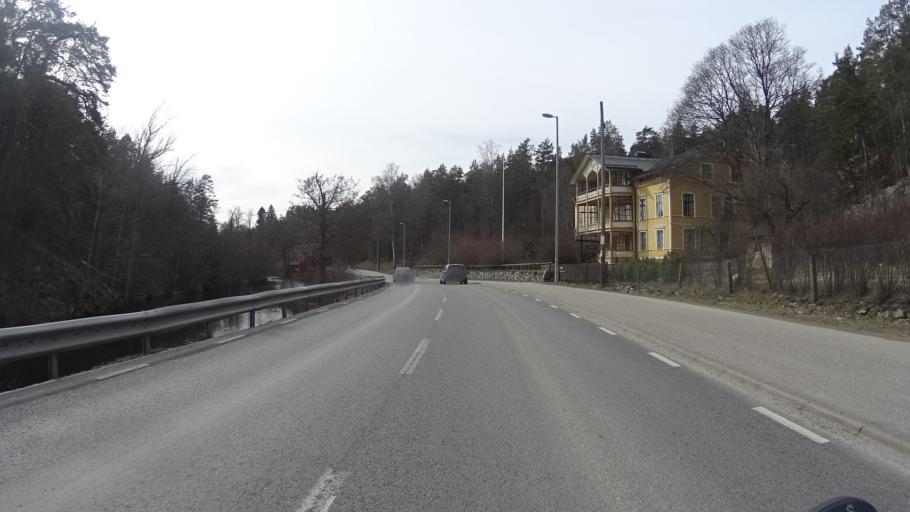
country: SE
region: Stockholm
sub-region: Nacka Kommun
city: Nacka
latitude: 59.2984
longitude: 18.1473
